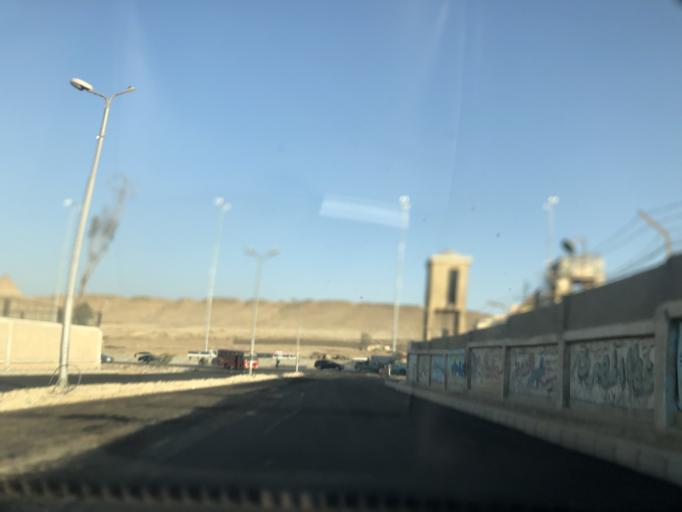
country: EG
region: Al Jizah
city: Al Jizah
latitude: 29.9793
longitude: 31.1131
